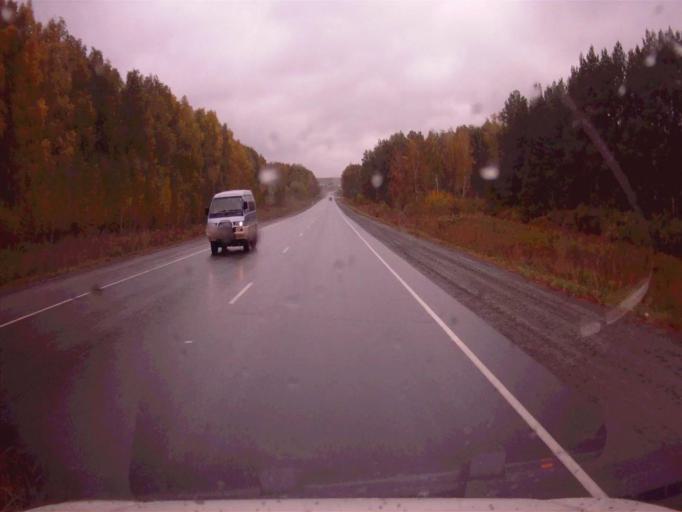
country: RU
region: Chelyabinsk
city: Roshchino
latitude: 55.3632
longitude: 61.2092
